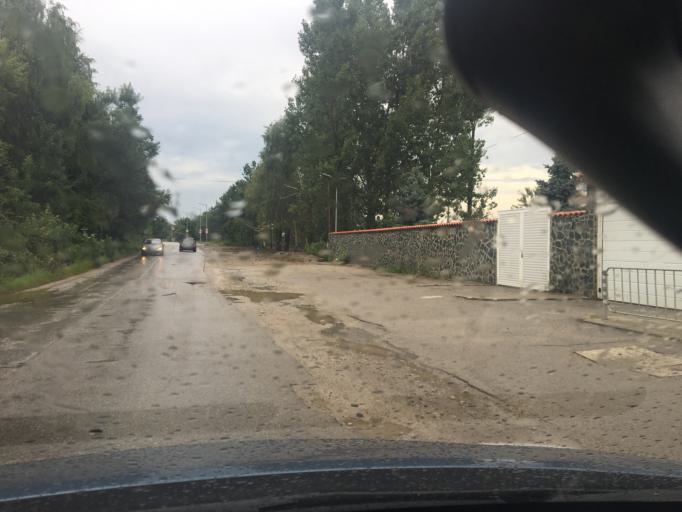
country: BG
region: Sofia-Capital
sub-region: Stolichna Obshtina
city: Sofia
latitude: 42.6401
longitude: 23.2949
